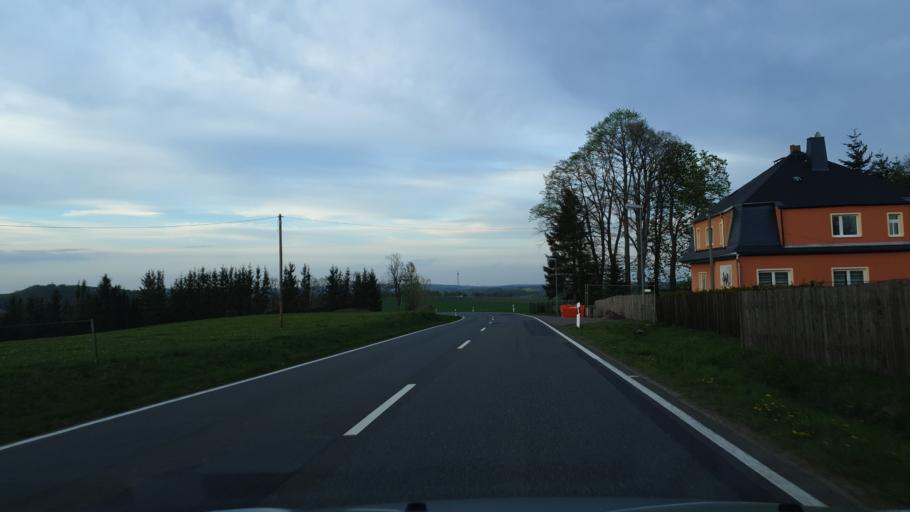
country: DE
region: Saxony
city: Oelsnitz
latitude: 50.7028
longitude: 12.6856
